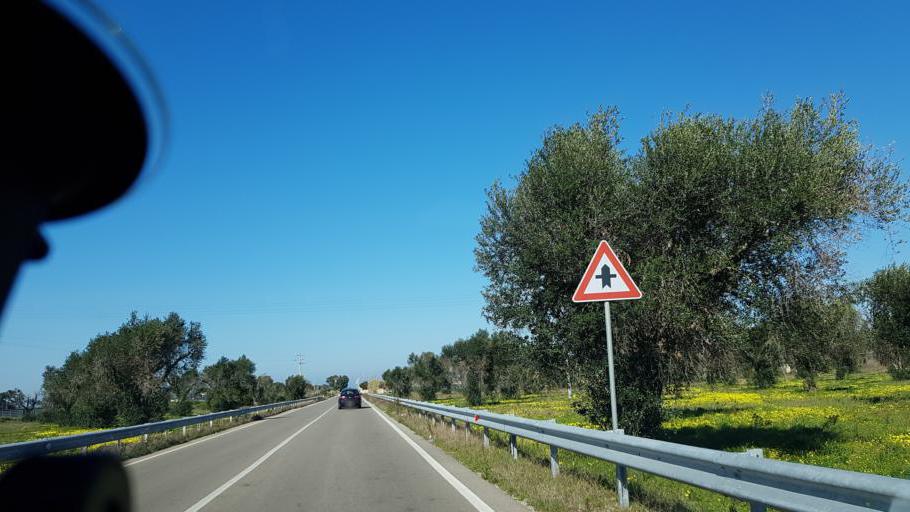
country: IT
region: Apulia
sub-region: Provincia di Brindisi
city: Torchiarolo
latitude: 40.5099
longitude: 18.0793
